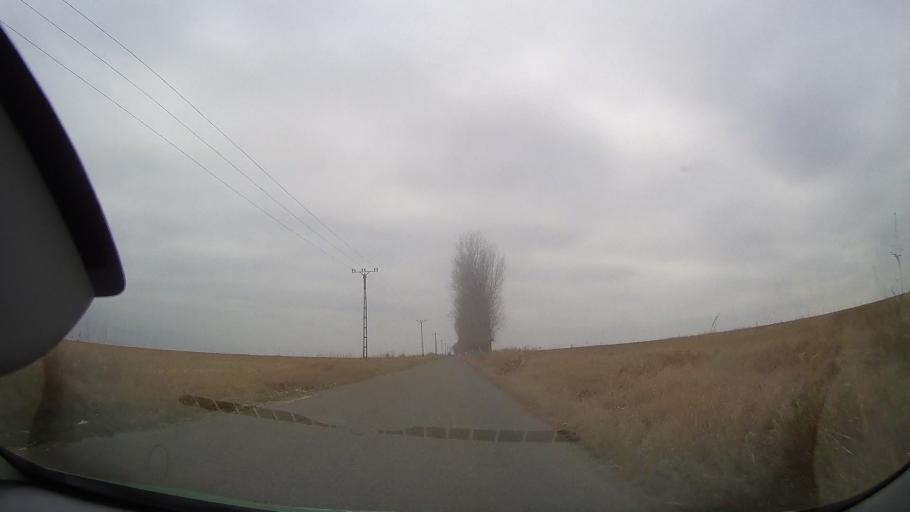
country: RO
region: Buzau
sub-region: Comuna Pogoanele
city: Pogoanele
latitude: 44.9494
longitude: 27.0133
